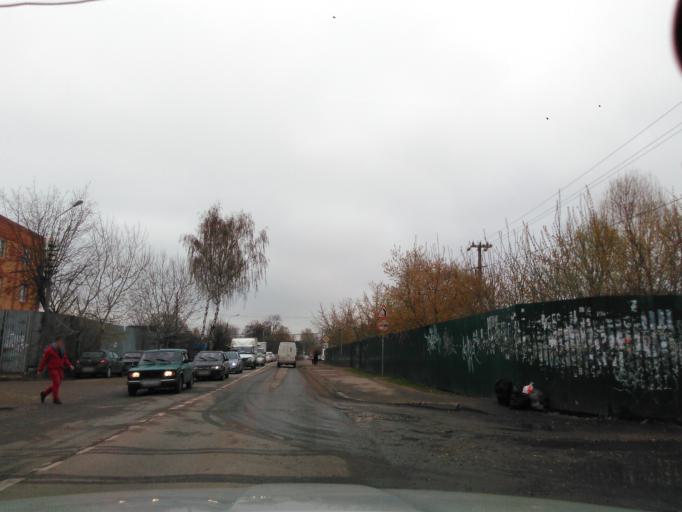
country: RU
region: Moskovskaya
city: Nakhabino
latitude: 55.8429
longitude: 37.1835
